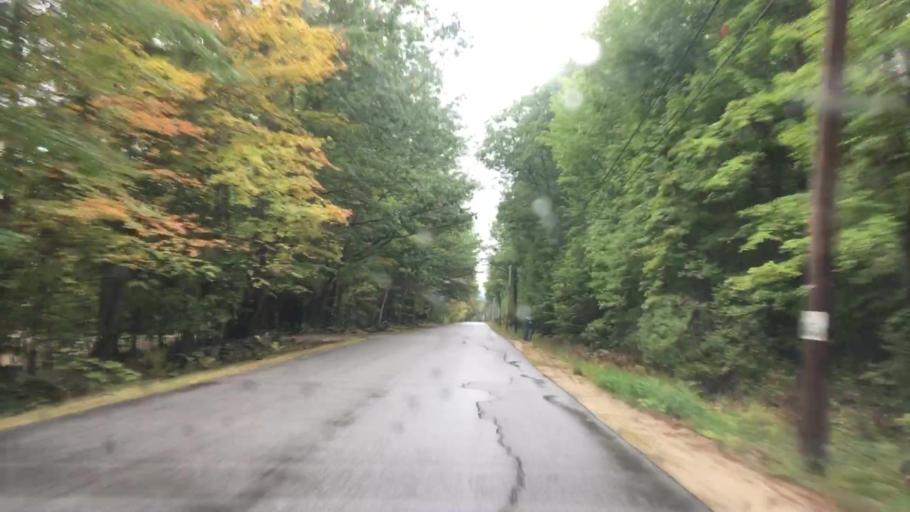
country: US
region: Maine
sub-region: Cumberland County
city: Harrison
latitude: 44.0687
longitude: -70.6322
